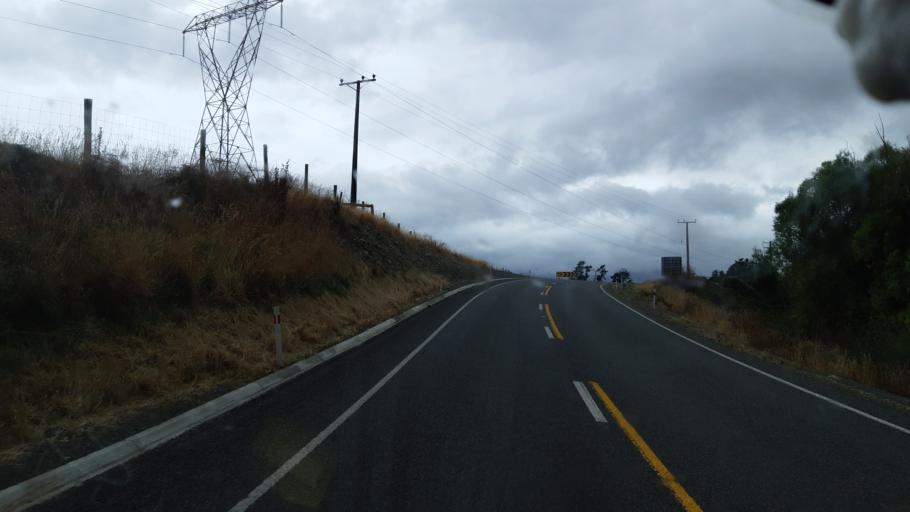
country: NZ
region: Canterbury
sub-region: Hurunui District
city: Amberley
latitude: -42.5891
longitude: 172.7771
